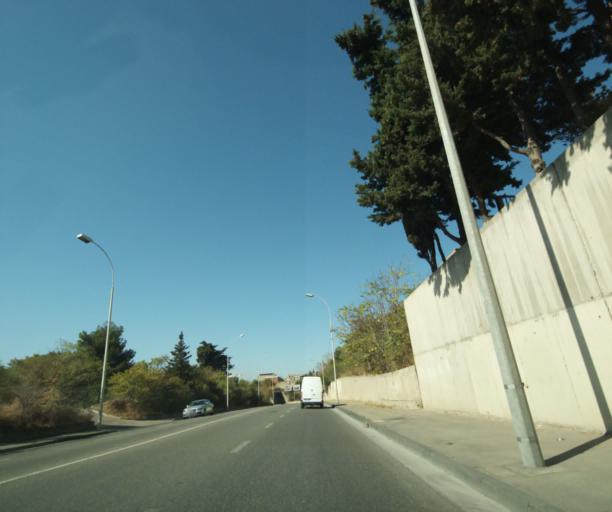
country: FR
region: Provence-Alpes-Cote d'Azur
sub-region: Departement des Bouches-du-Rhone
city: Marseille 14
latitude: 43.3396
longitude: 5.3908
